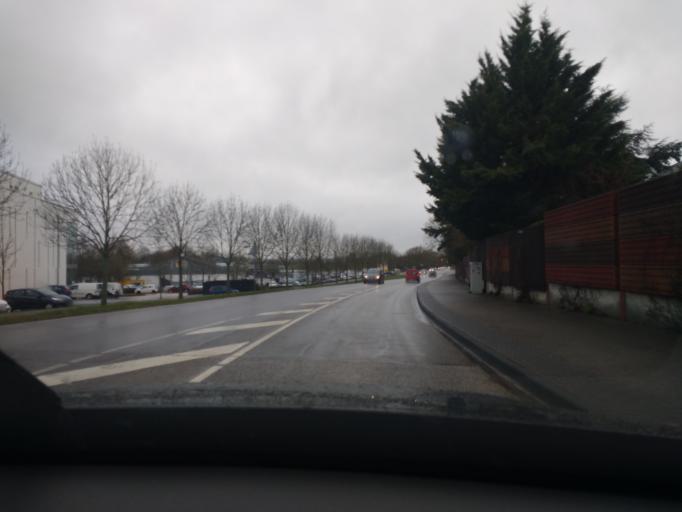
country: DE
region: Rheinland-Pfalz
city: Irsch
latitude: 49.7389
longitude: 6.6976
